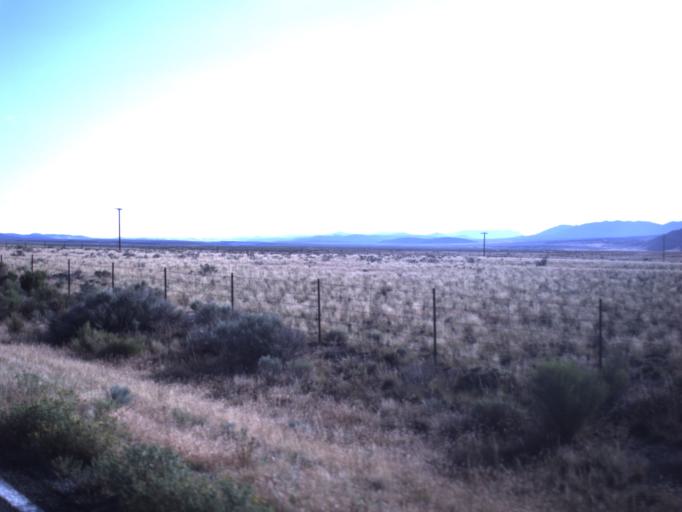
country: US
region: Utah
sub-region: Iron County
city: Enoch
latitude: 37.8880
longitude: -113.0316
